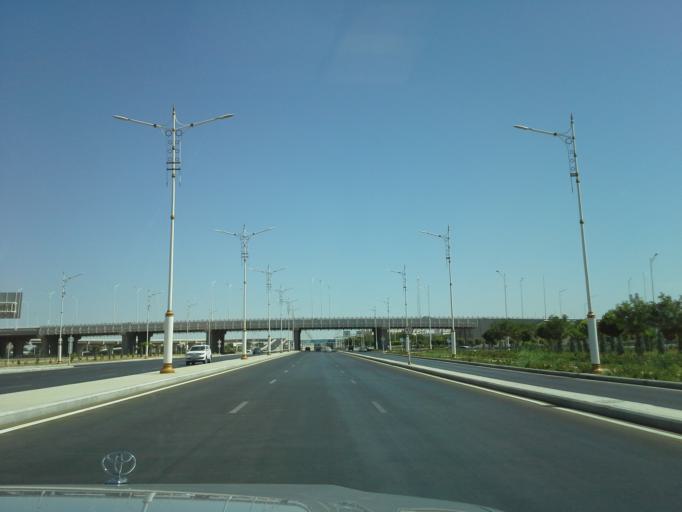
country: TM
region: Ahal
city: Ashgabat
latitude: 37.9281
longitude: 58.4249
